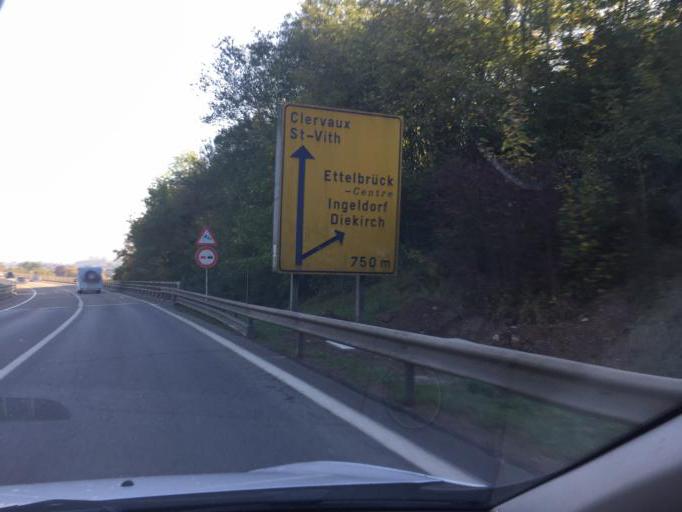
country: LU
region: Diekirch
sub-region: Canton de Diekirch
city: Ettelbruck
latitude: 49.8471
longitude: 6.1165
